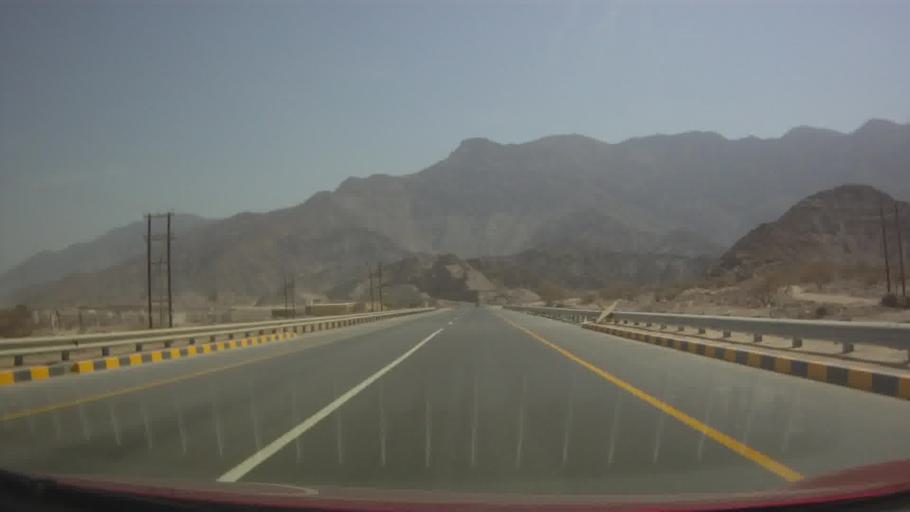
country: OM
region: Muhafazat Masqat
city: Muscat
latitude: 23.4042
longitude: 58.7807
